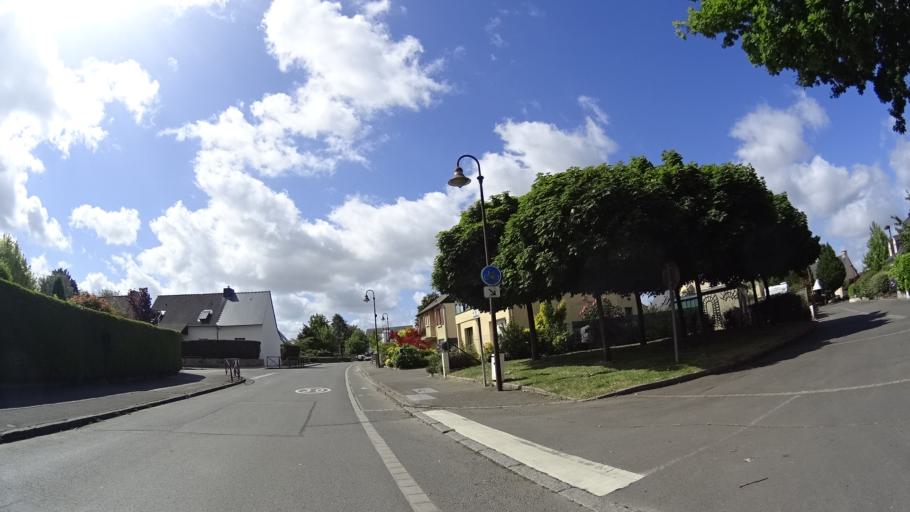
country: FR
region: Brittany
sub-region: Departement d'Ille-et-Vilaine
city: La Meziere
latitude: 48.2216
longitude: -1.7547
